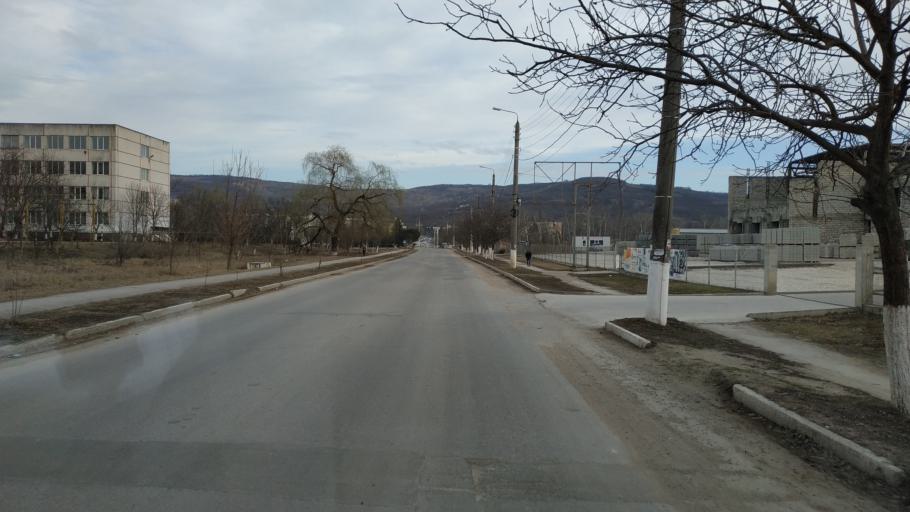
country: MD
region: Nisporeni
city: Nisporeni
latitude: 47.0829
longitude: 28.1778
